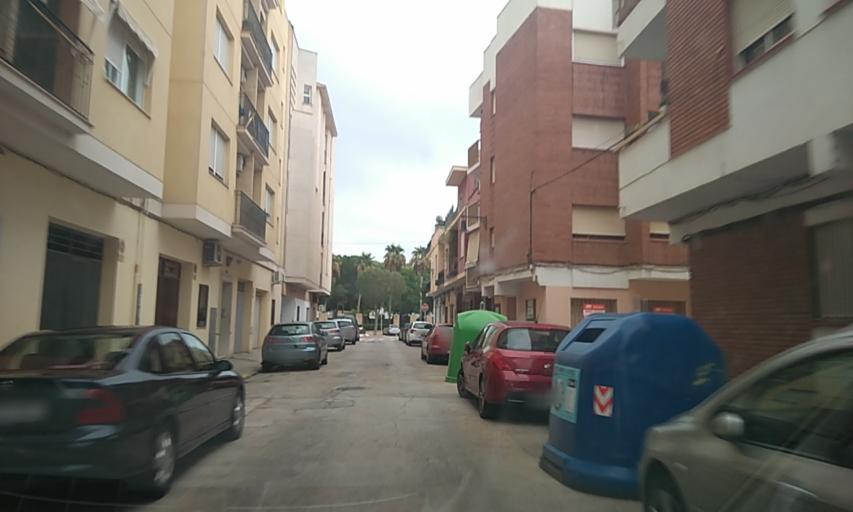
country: ES
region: Valencia
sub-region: Provincia de Valencia
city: L'Alcudia
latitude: 39.1920
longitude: -0.5088
